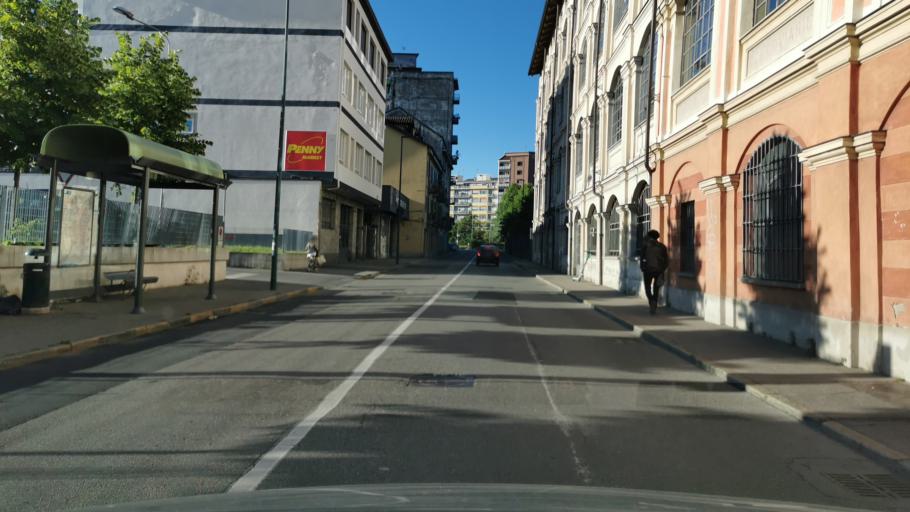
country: IT
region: Piedmont
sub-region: Provincia di Torino
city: Turin
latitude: 45.0890
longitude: 7.6565
